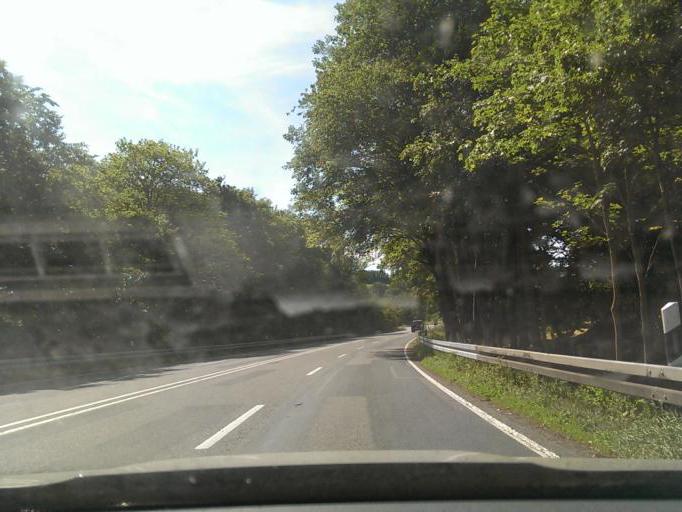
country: DE
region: Lower Saxony
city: Alfeld
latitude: 51.9870
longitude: 9.8034
